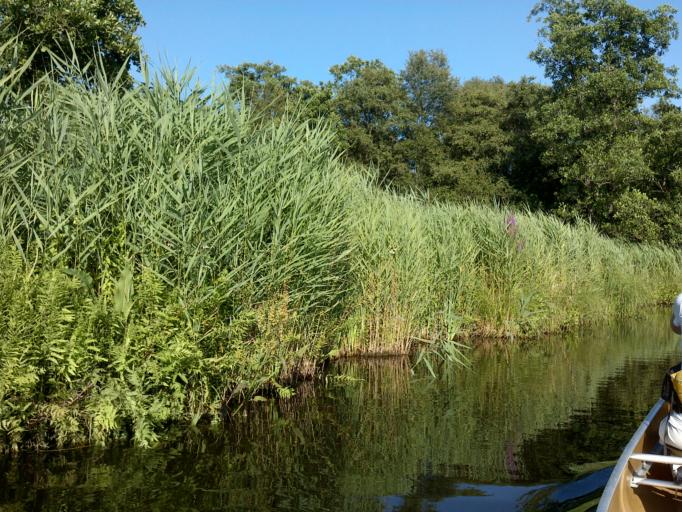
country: NL
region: Overijssel
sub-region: Gemeente Steenwijkerland
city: Sint Jansklooster
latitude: 52.6700
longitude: 6.0302
